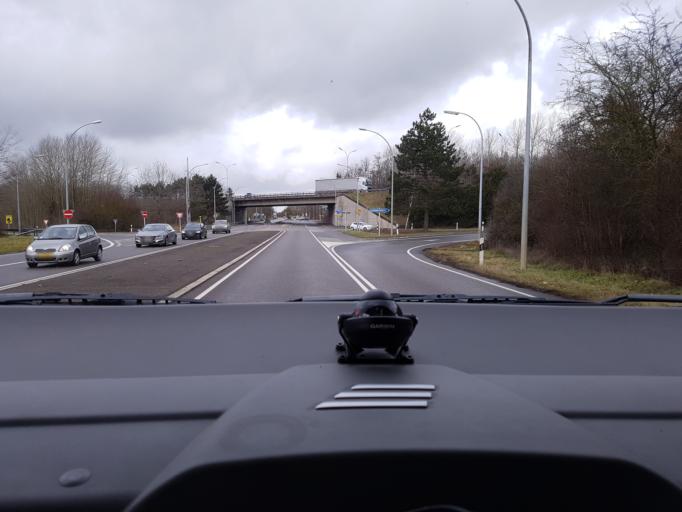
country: LU
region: Luxembourg
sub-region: Canton de Capellen
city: Mamer
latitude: 49.6376
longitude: 6.0097
